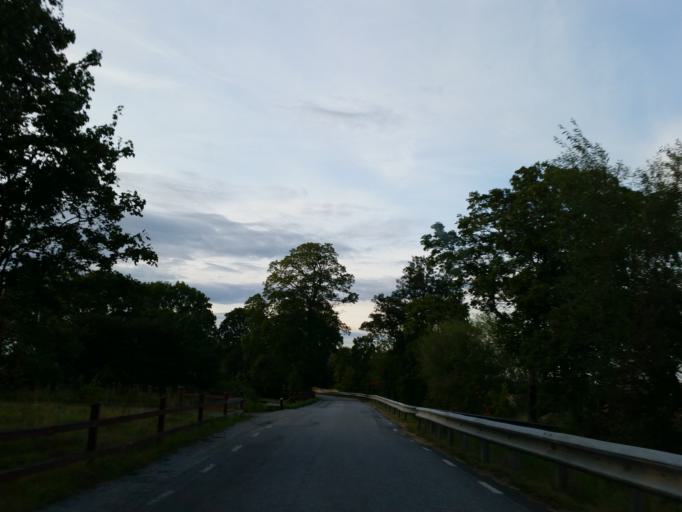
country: SE
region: Stockholm
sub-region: Sigtuna Kommun
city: Marsta
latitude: 59.6319
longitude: 17.8818
